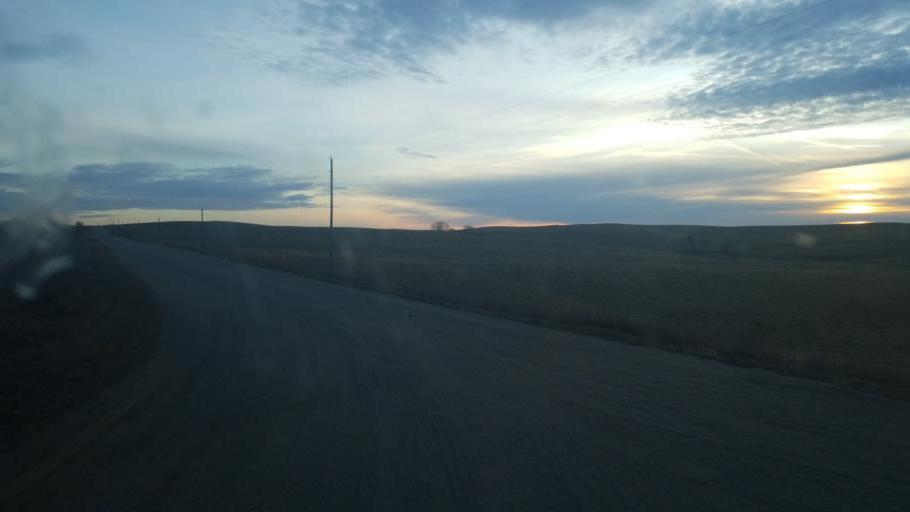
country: US
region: Nebraska
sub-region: Knox County
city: Center
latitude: 42.6845
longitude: -97.7597
